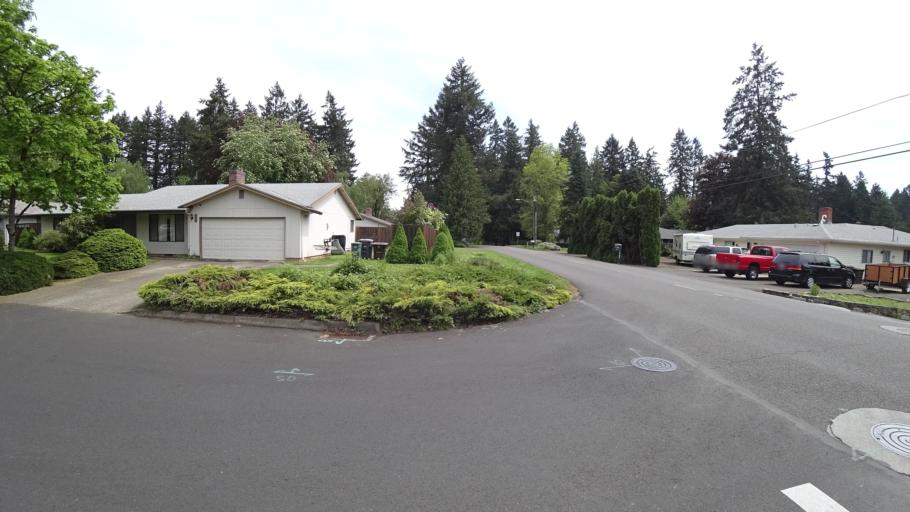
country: US
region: Oregon
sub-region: Washington County
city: Hillsboro
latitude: 45.5123
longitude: -122.9452
